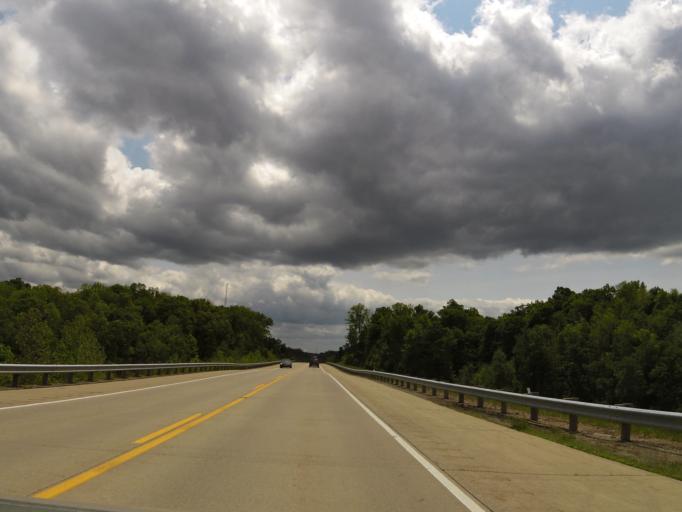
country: US
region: Ohio
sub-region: Meigs County
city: Pomeroy
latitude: 39.1816
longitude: -82.0477
